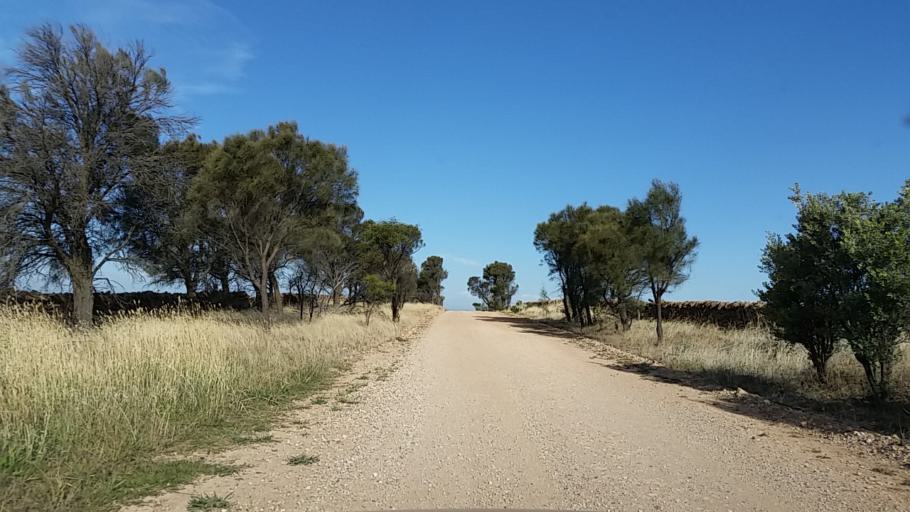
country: AU
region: South Australia
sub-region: Barossa
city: Angaston
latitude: -34.6153
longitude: 139.2002
